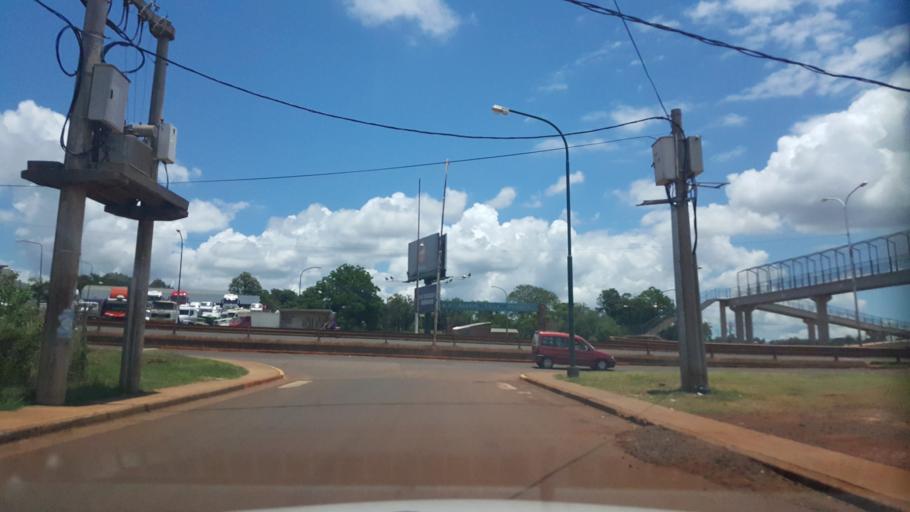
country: AR
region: Misiones
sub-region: Departamento de Capital
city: Posadas
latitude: -27.4215
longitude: -55.8987
